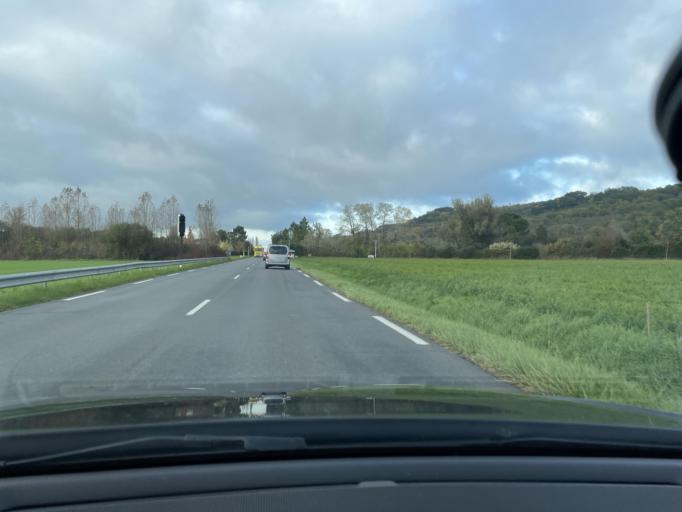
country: FR
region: Aquitaine
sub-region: Departement du Lot-et-Garonne
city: Casteljaloux
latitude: 44.3468
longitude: 0.1074
